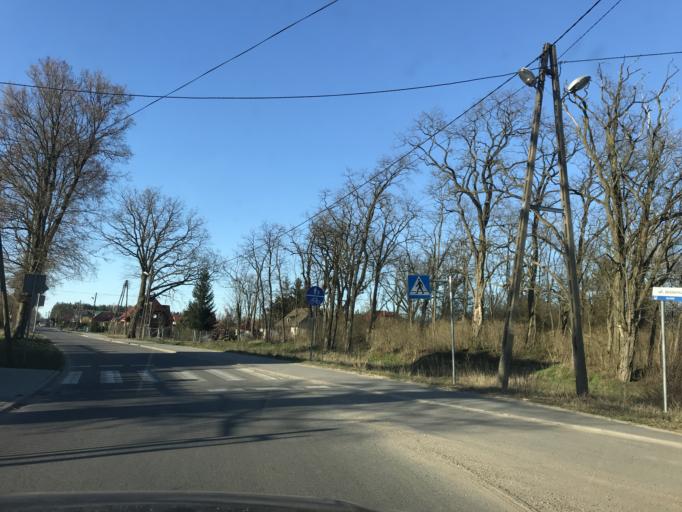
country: PL
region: Lubusz
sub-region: Powiat gorzowski
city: Deszczno
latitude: 52.6495
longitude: 15.3163
